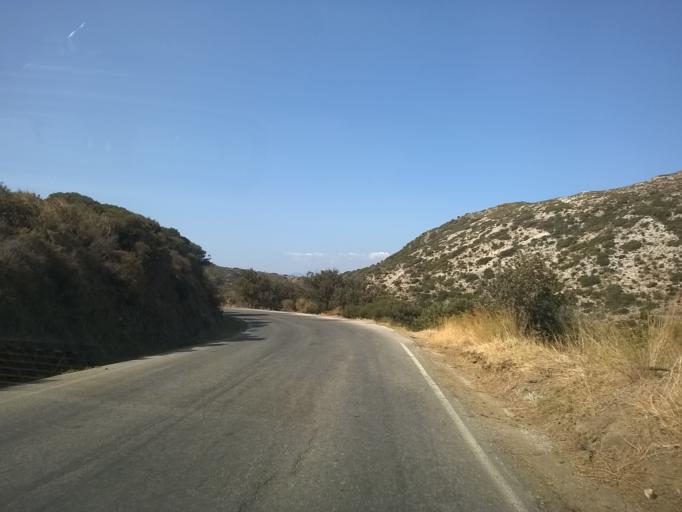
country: GR
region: South Aegean
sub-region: Nomos Kykladon
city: Filotion
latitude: 37.0776
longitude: 25.4918
